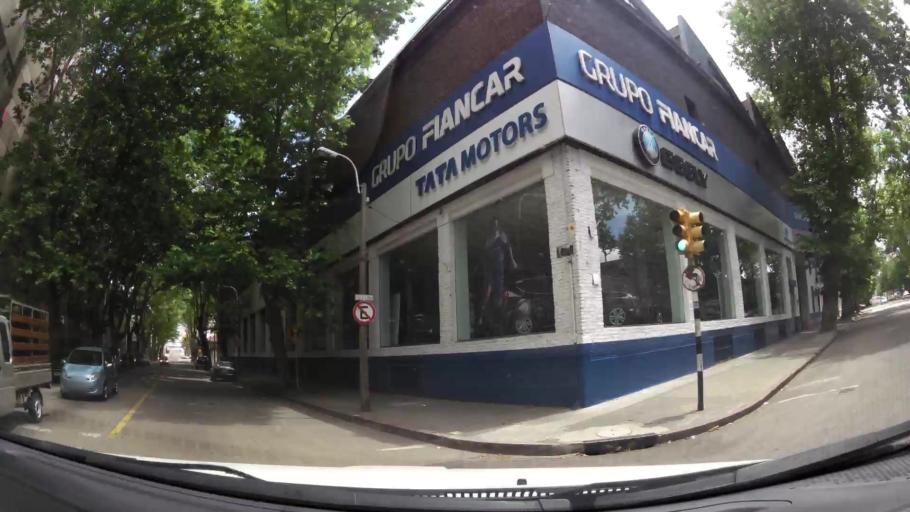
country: UY
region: Montevideo
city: Montevideo
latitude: -34.8904
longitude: -56.1931
